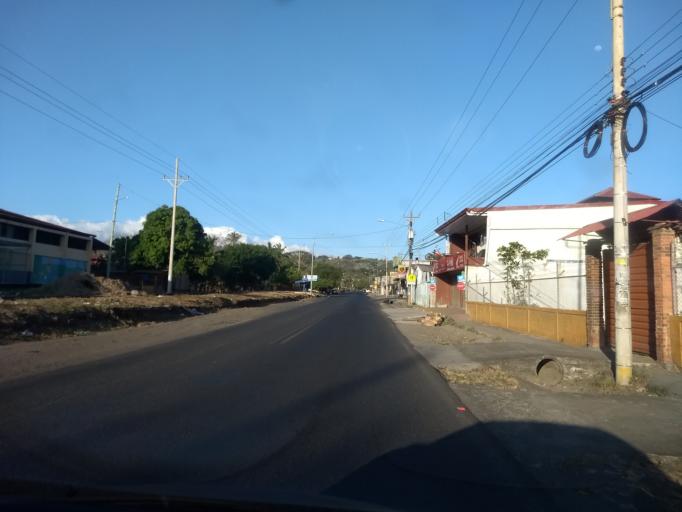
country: CR
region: Puntarenas
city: Esparza
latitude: 9.9877
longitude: -84.7148
